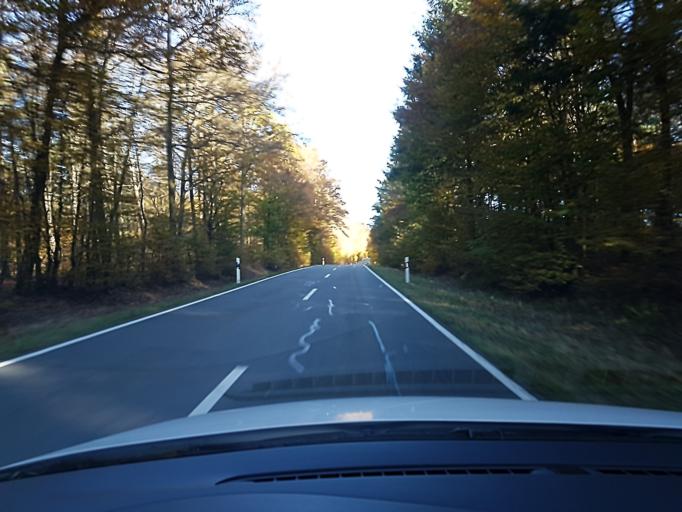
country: DE
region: Baden-Wuerttemberg
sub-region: Karlsruhe Region
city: Fahrenbach
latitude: 49.4087
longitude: 9.1878
